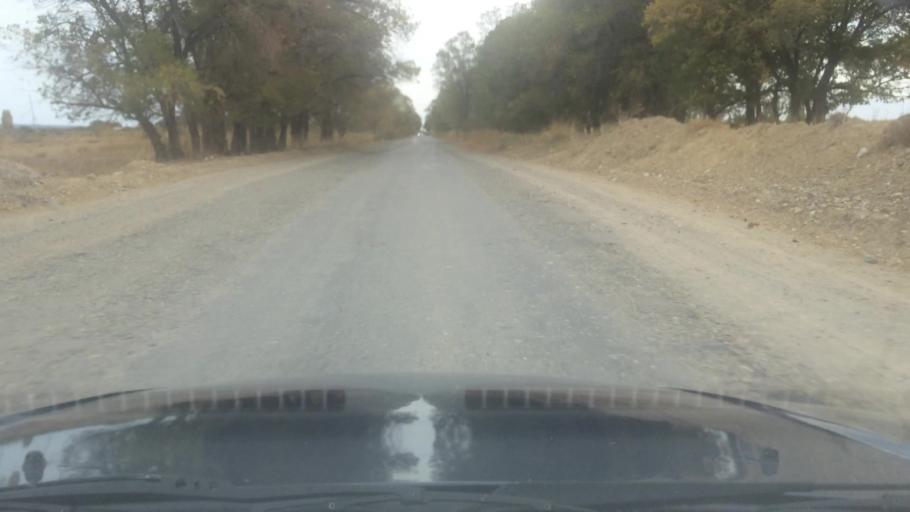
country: KG
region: Ysyk-Koel
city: Balykchy
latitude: 42.3053
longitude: 76.4729
